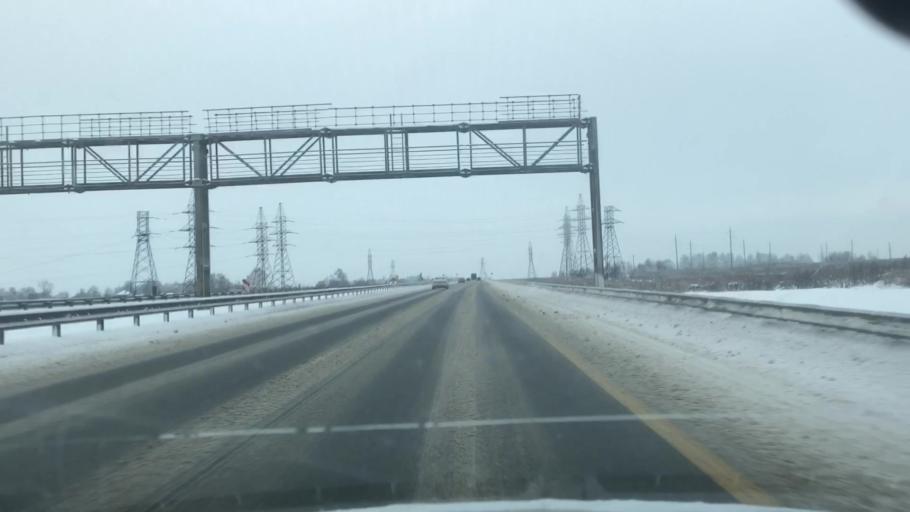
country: RU
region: Moskovskaya
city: Mikhnevo
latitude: 55.1232
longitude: 37.9324
